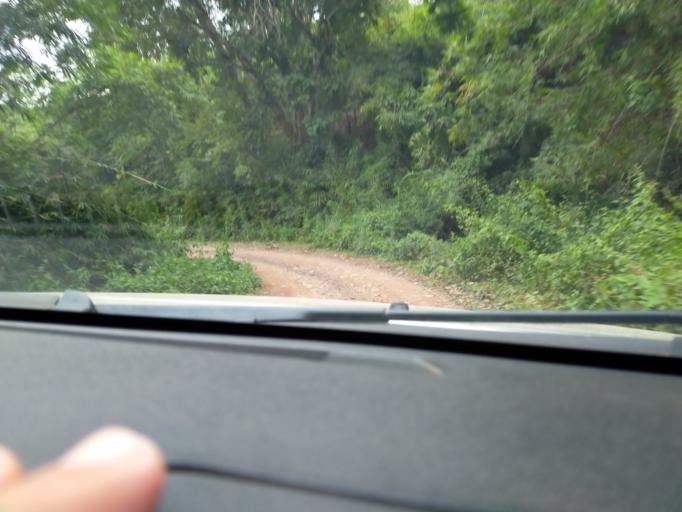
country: TH
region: Nan
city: Chaloem Phra Kiat
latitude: 19.7939
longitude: 101.3608
